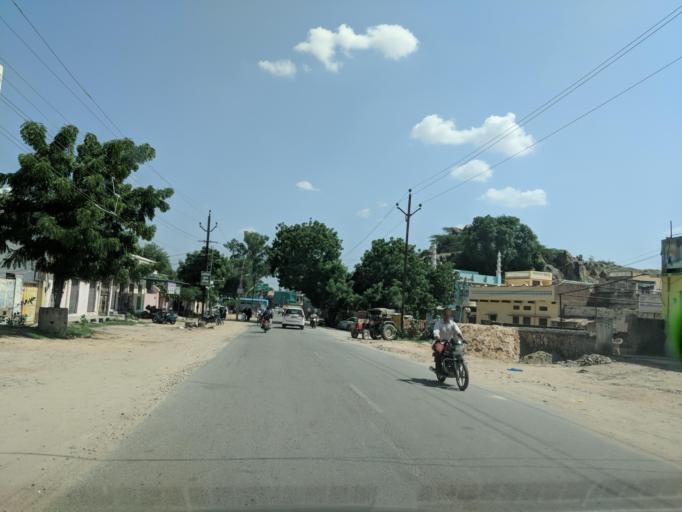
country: IN
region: Rajasthan
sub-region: Jhunjhunun
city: Jhunjhunun
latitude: 28.1351
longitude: 75.3901
